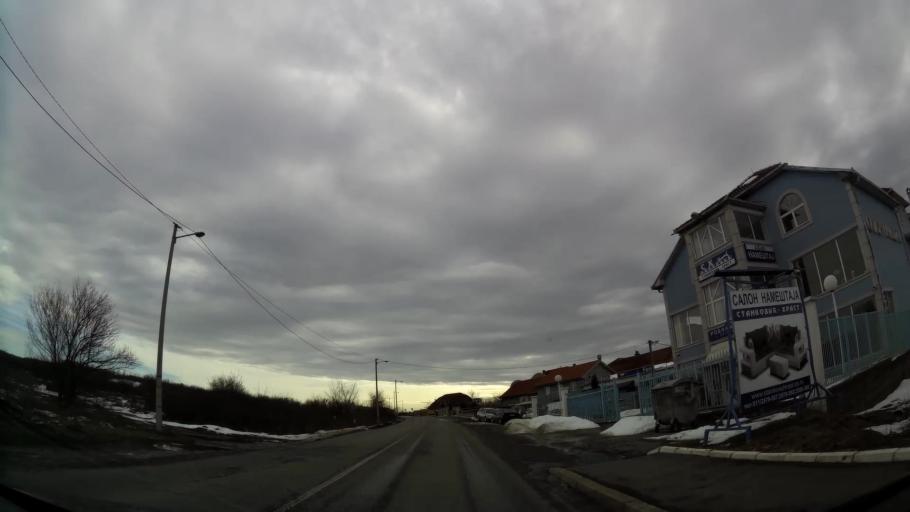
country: RS
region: Central Serbia
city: Sremcica
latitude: 44.7282
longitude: 20.3884
